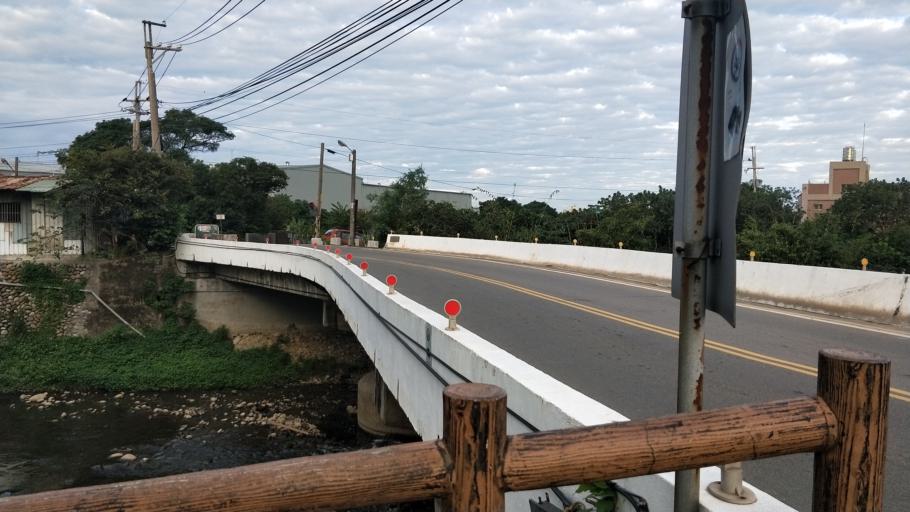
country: TW
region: Taiwan
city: Taoyuan City
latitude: 24.9807
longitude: 121.2334
